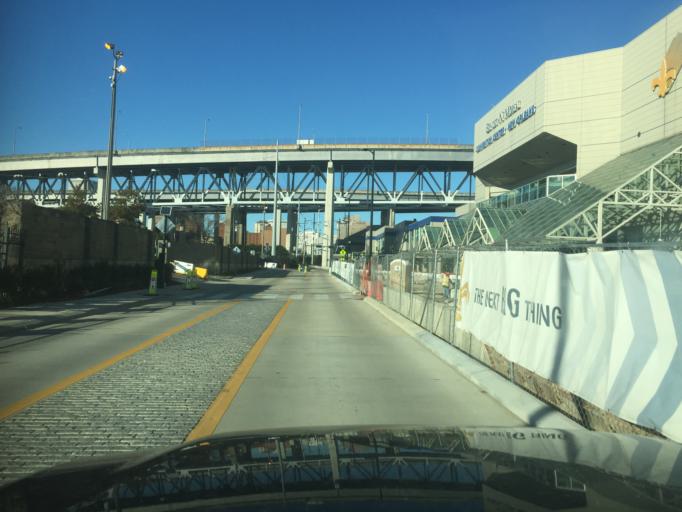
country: US
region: Louisiana
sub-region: Orleans Parish
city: New Orleans
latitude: 29.9361
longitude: -90.0642
